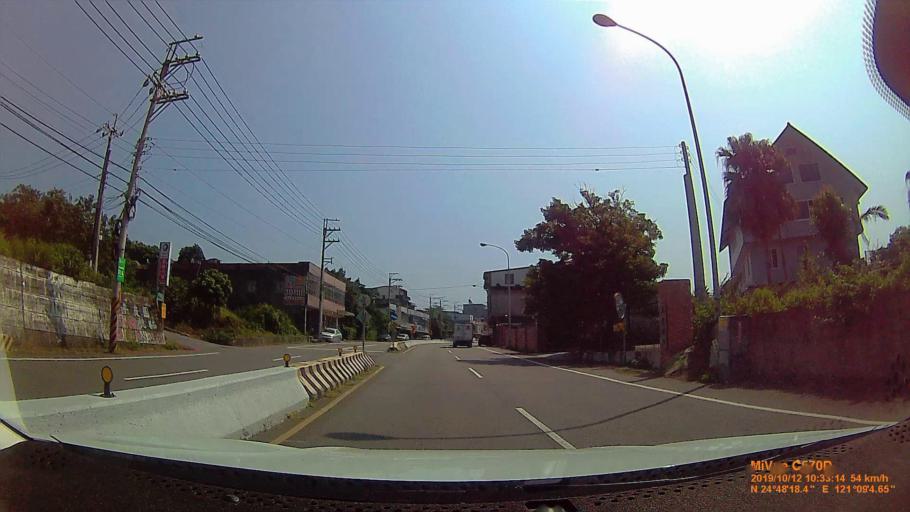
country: TW
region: Taiwan
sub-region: Hsinchu
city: Zhubei
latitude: 24.8051
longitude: 121.1513
